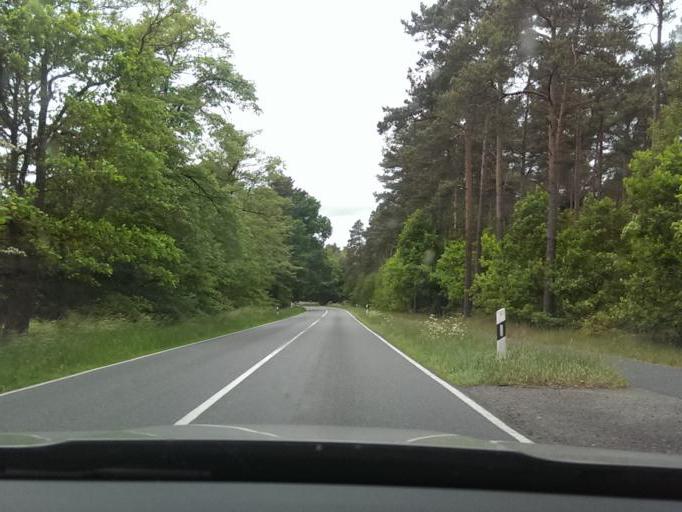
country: DE
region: Lower Saxony
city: Wietze
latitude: 52.6925
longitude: 9.8493
